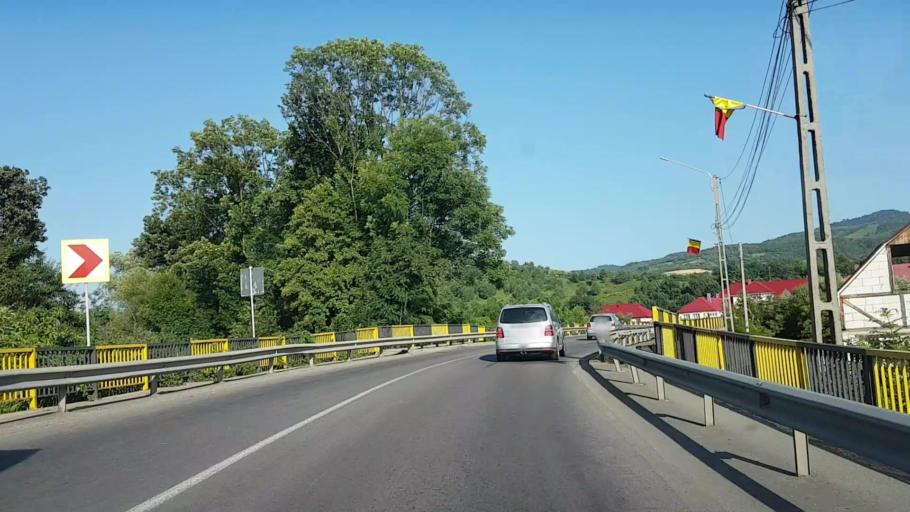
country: RO
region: Bistrita-Nasaud
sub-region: Comuna Josenii Bargaului
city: Josenii Bargaului
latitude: 47.2128
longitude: 24.6755
